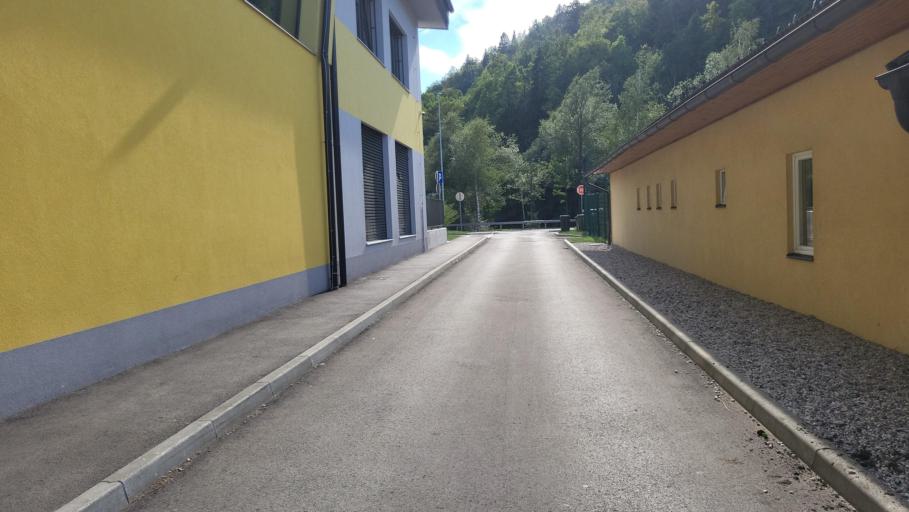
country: SI
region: Ziri
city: Ziri
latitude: 46.0454
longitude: 14.1069
